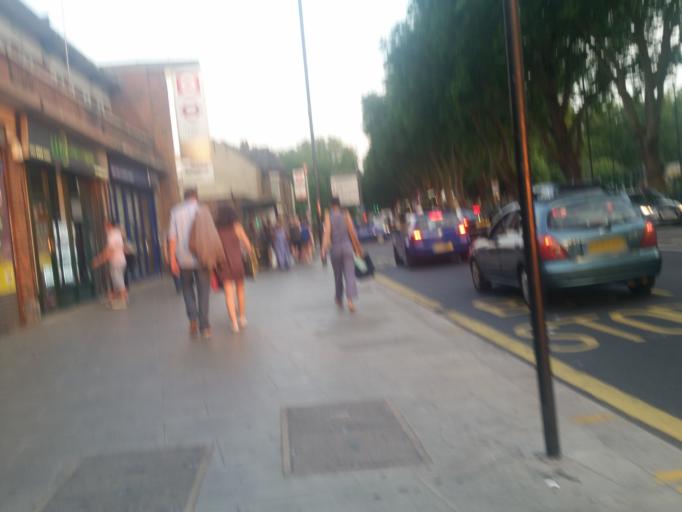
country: GB
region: England
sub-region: Greater London
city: Harringay
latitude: 51.5899
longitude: -0.1026
